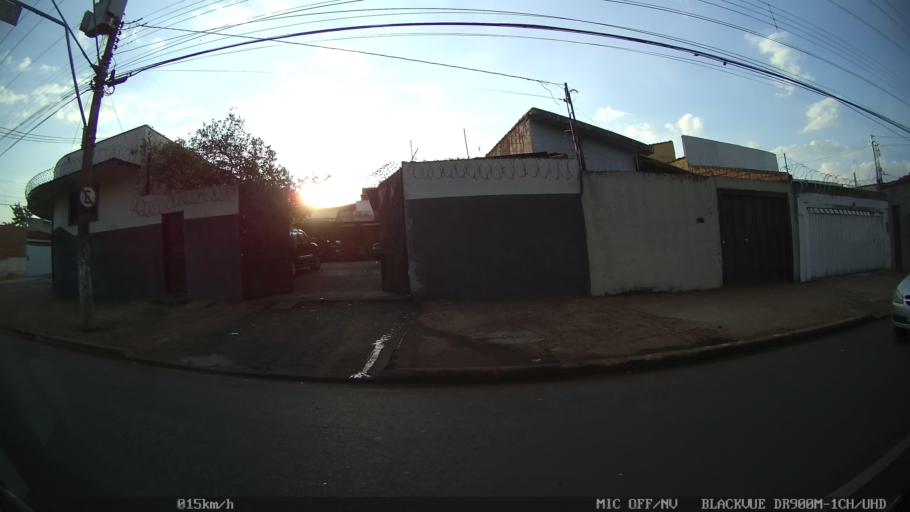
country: BR
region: Sao Paulo
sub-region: Ribeirao Preto
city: Ribeirao Preto
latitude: -21.1472
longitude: -47.8067
